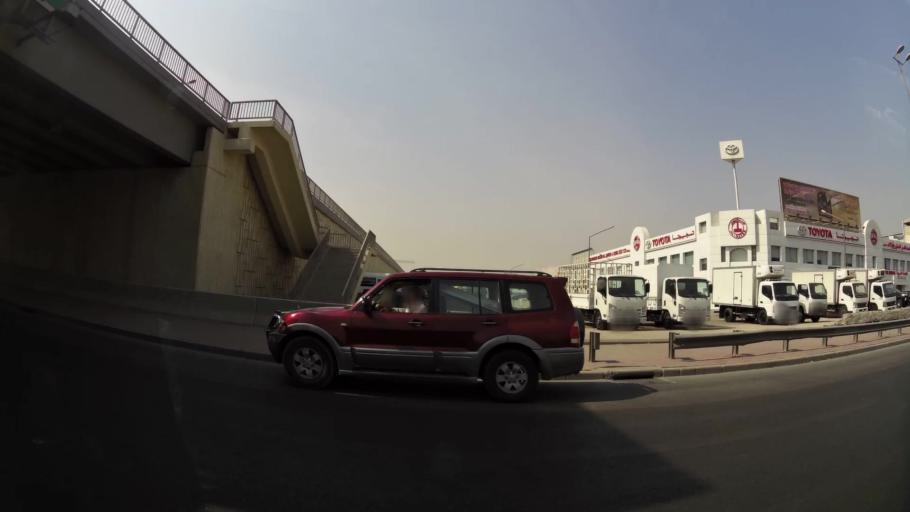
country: KW
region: Al Asimah
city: Ar Rabiyah
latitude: 29.3064
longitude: 47.9441
